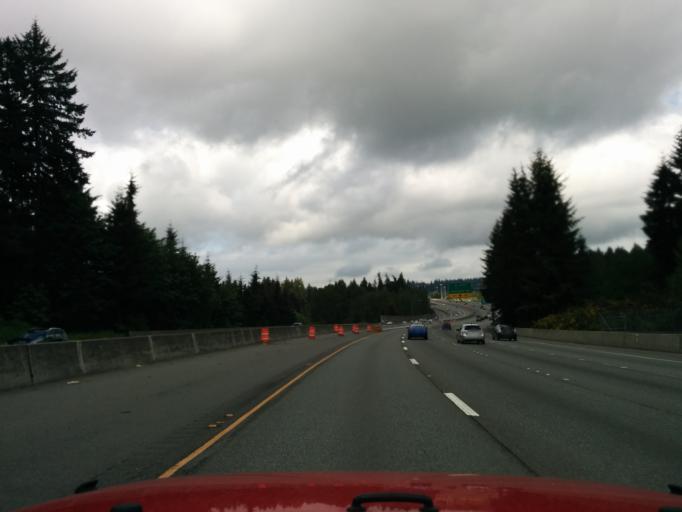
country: US
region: Washington
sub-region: Snohomish County
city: Martha Lake
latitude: 47.8241
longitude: -122.2520
